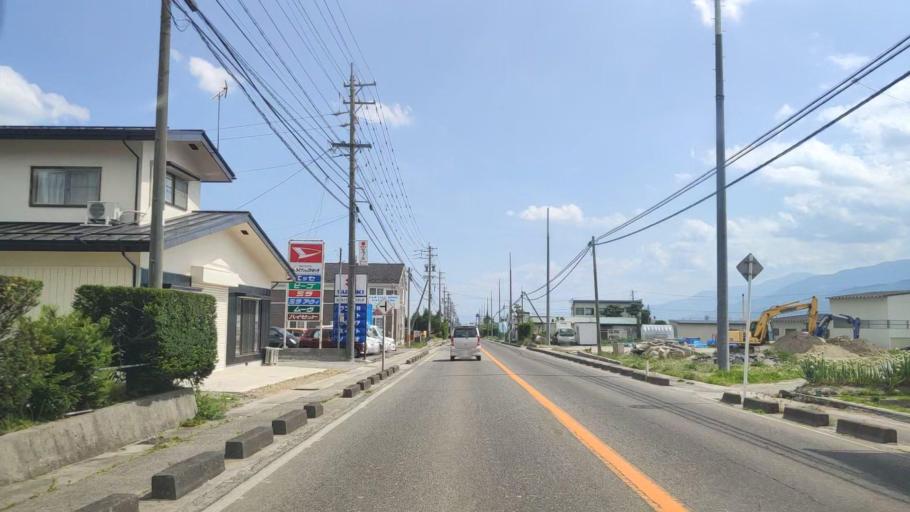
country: JP
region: Nagano
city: Omachi
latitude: 36.4635
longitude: 137.8498
